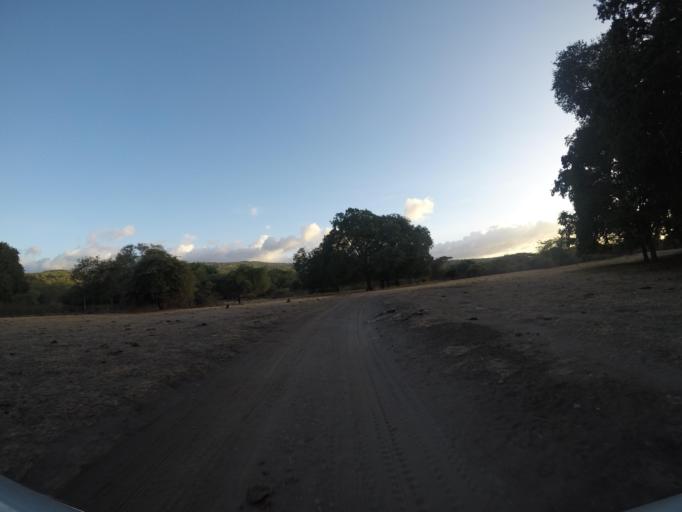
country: TL
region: Lautem
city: Lospalos
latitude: -8.3251
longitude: 126.9930
